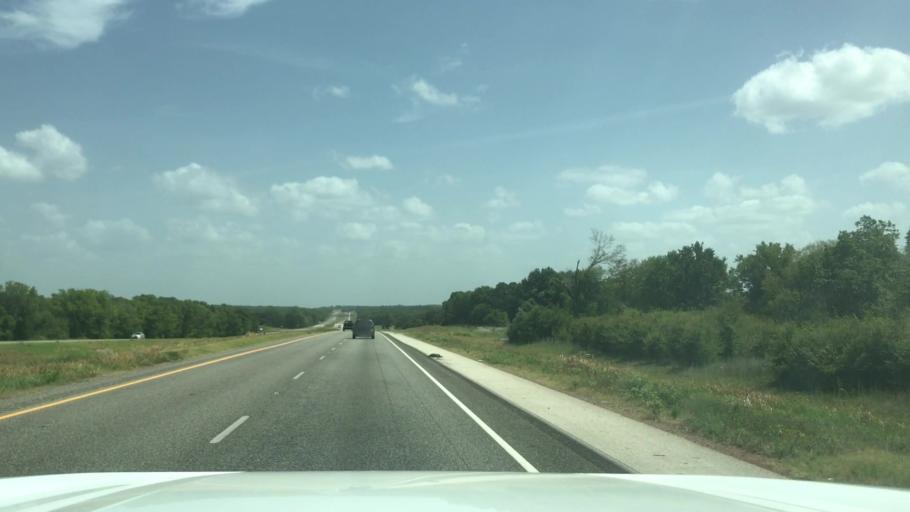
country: US
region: Texas
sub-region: Robertson County
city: Calvert
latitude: 30.9555
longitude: -96.6550
